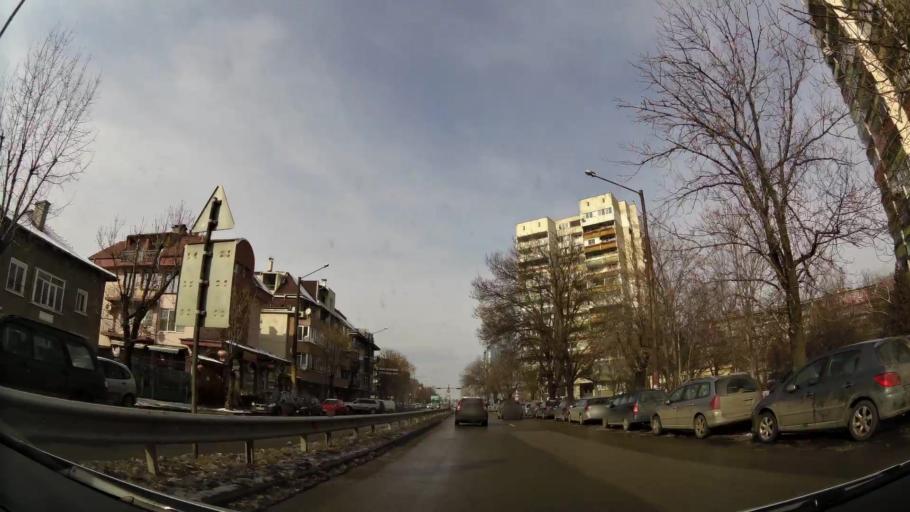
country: BG
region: Sofia-Capital
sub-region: Stolichna Obshtina
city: Sofia
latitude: 42.7082
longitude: 23.3570
